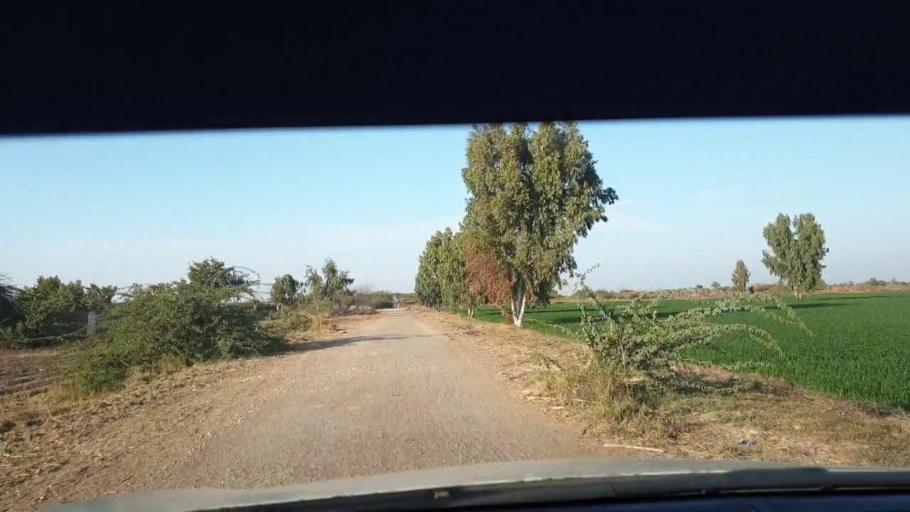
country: PK
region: Sindh
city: Berani
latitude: 25.8209
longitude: 68.9098
